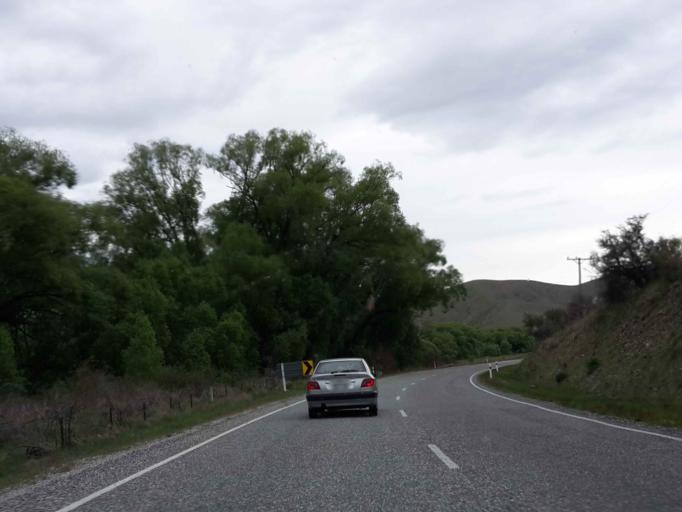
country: NZ
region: Otago
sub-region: Queenstown-Lakes District
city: Wanaka
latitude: -44.7162
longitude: 169.5038
